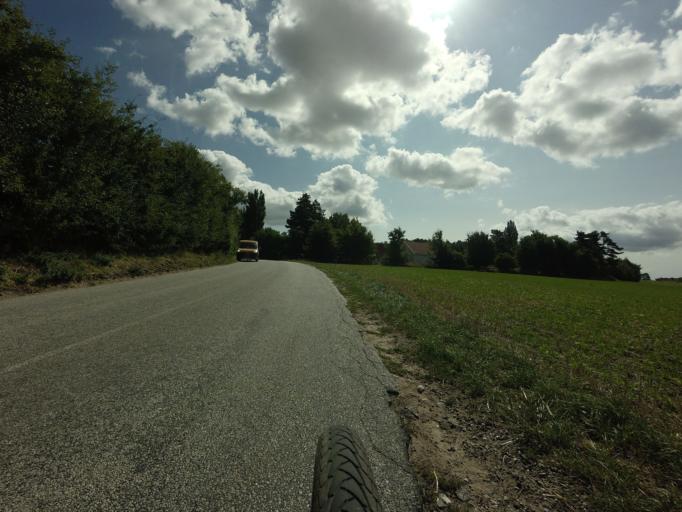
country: DK
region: Zealand
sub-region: Vordingborg Kommune
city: Stege
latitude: 54.9720
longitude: 12.4560
